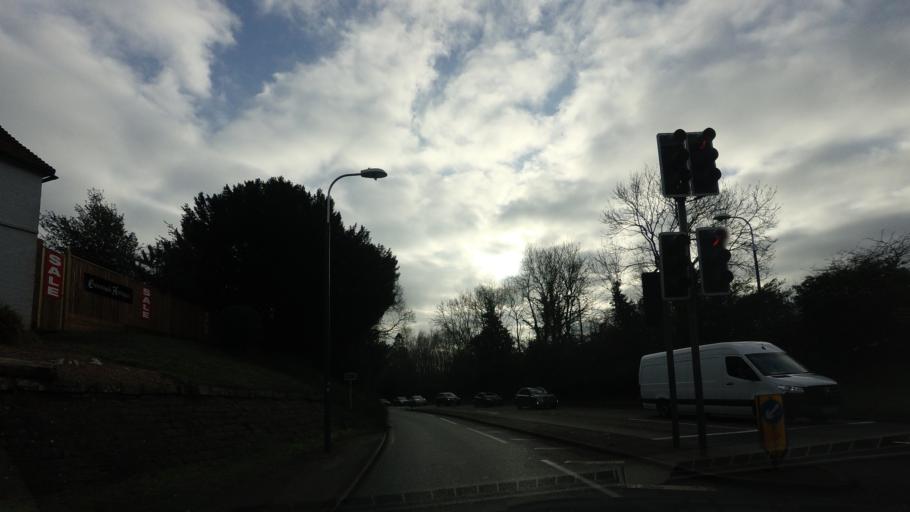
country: GB
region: England
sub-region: Kent
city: Hawkhurst
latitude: 51.0543
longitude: 0.4460
